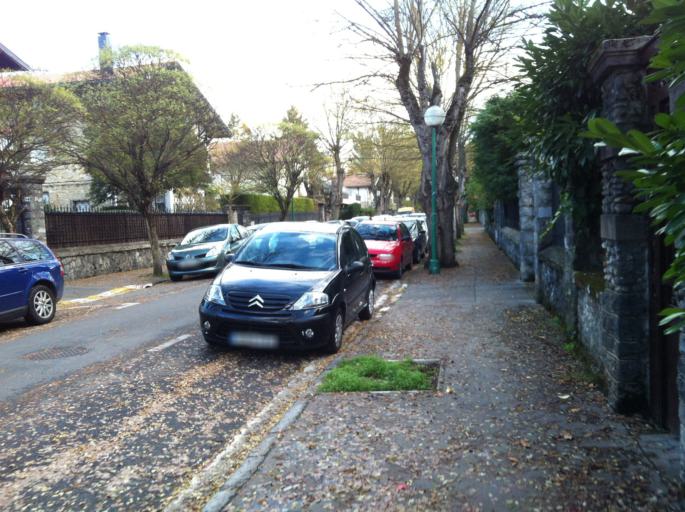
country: ES
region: Basque Country
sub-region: Provincia de Alava
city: Gasteiz / Vitoria
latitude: 42.8382
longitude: -2.6774
